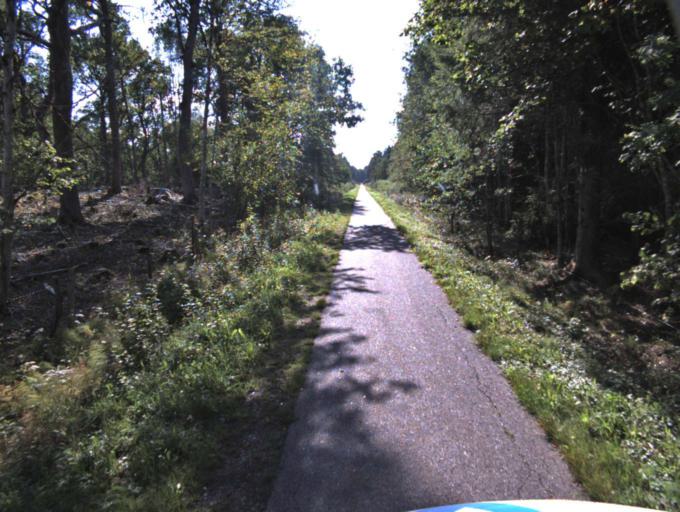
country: SE
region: Vaestra Goetaland
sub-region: Boras Kommun
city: Dalsjofors
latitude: 57.8322
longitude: 13.2197
